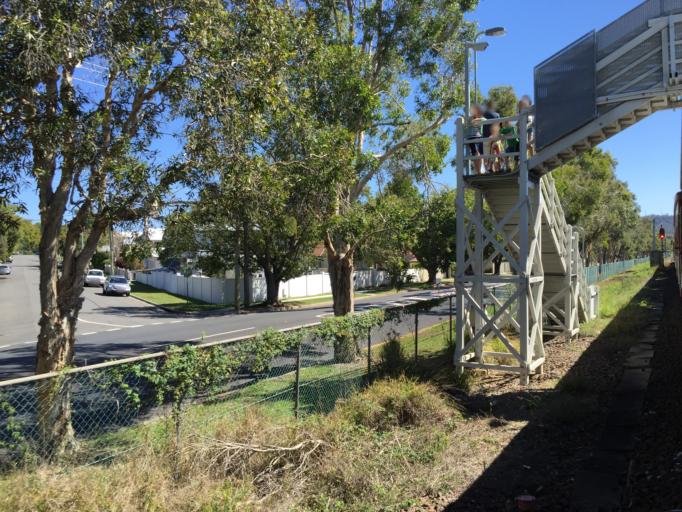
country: AU
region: Queensland
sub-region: Brisbane
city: Taringa
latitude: -27.5181
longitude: 152.9747
